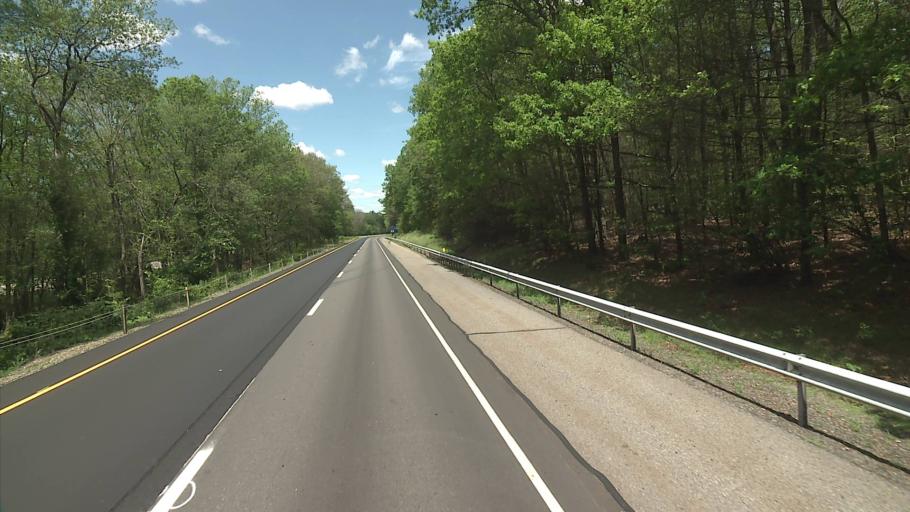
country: US
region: Connecticut
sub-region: Windham County
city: Killingly Center
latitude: 41.8257
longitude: -71.8728
